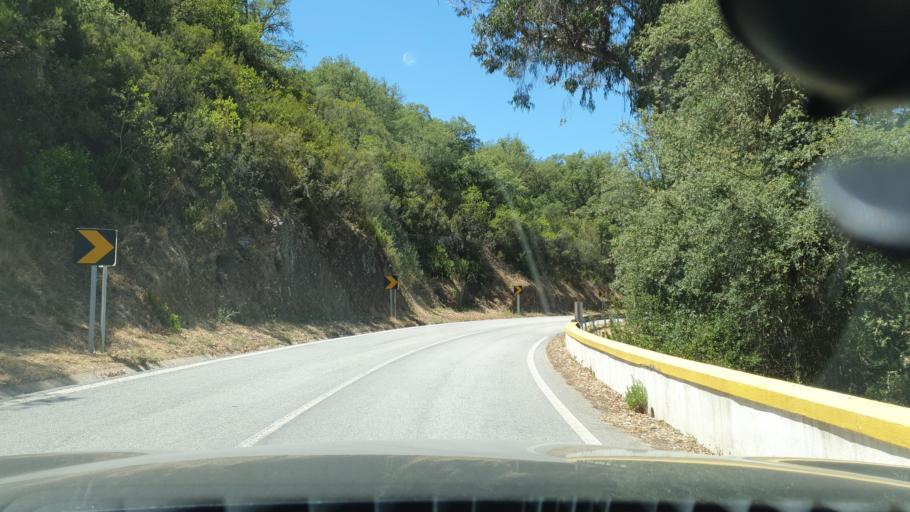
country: PT
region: Beja
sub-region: Odemira
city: Odemira
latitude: 37.5749
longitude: -8.4901
